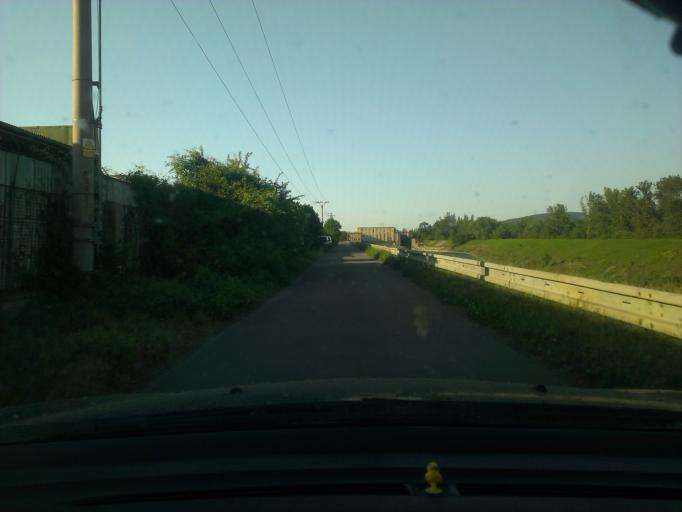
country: SK
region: Trnavsky
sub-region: Okres Trnava
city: Piestany
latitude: 48.6554
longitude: 17.8524
